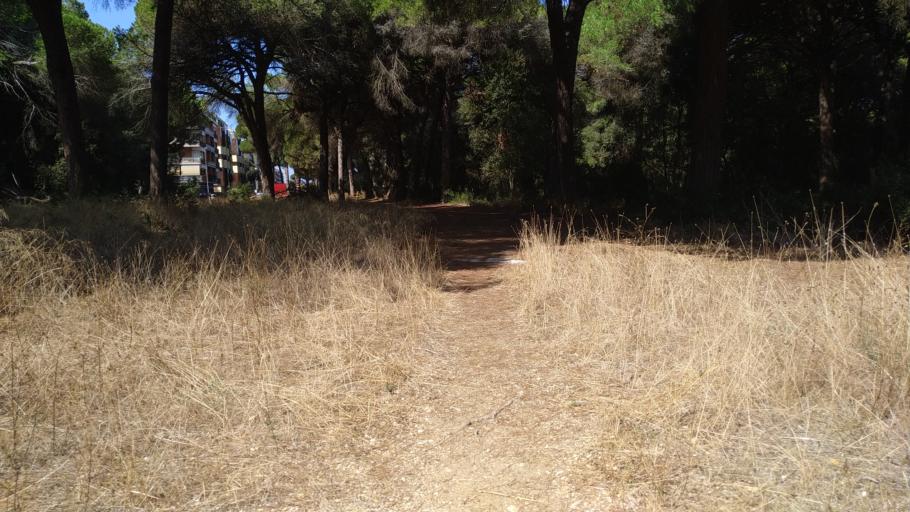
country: IT
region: Latium
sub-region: Citta metropolitana di Roma Capitale
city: Lido di Ostia
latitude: 41.7333
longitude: 12.3037
